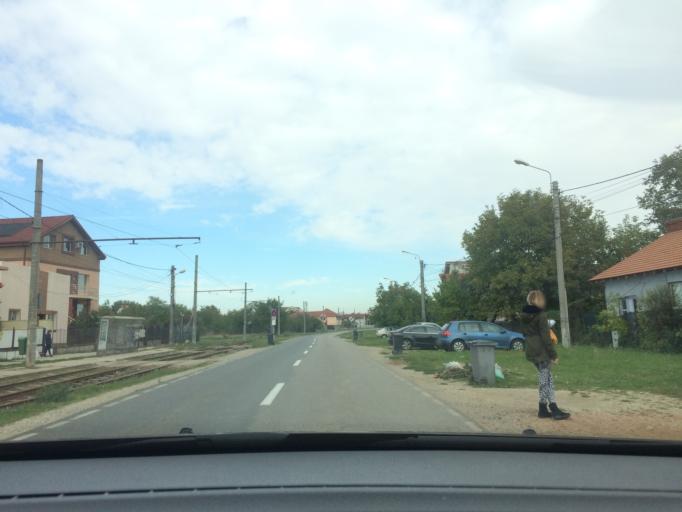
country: RO
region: Timis
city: Timisoara
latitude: 45.7555
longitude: 21.1920
